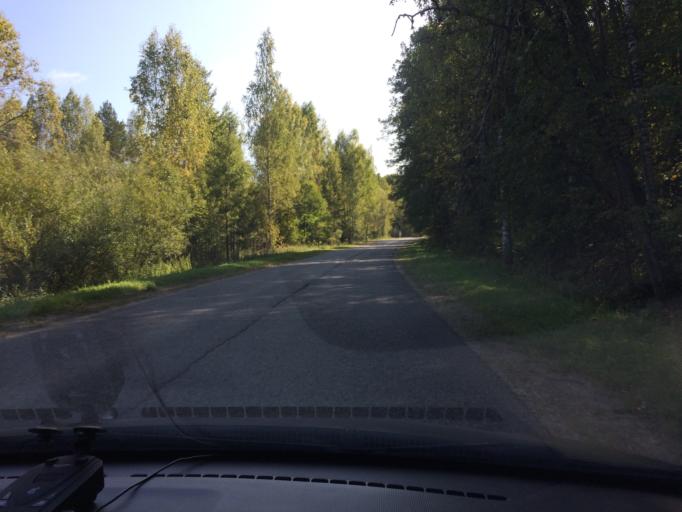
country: RU
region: Mariy-El
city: Surok
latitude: 56.5660
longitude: 48.2945
